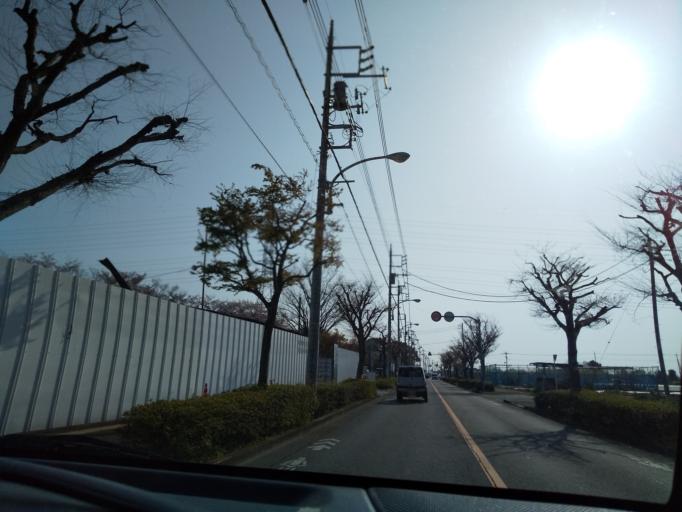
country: JP
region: Tokyo
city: Fussa
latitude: 35.7286
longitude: 139.3012
